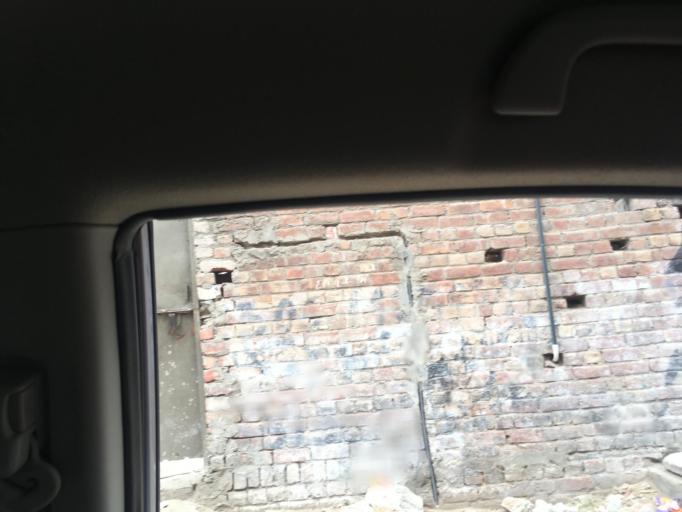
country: PK
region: Punjab
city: Lahore
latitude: 31.6198
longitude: 74.3471
